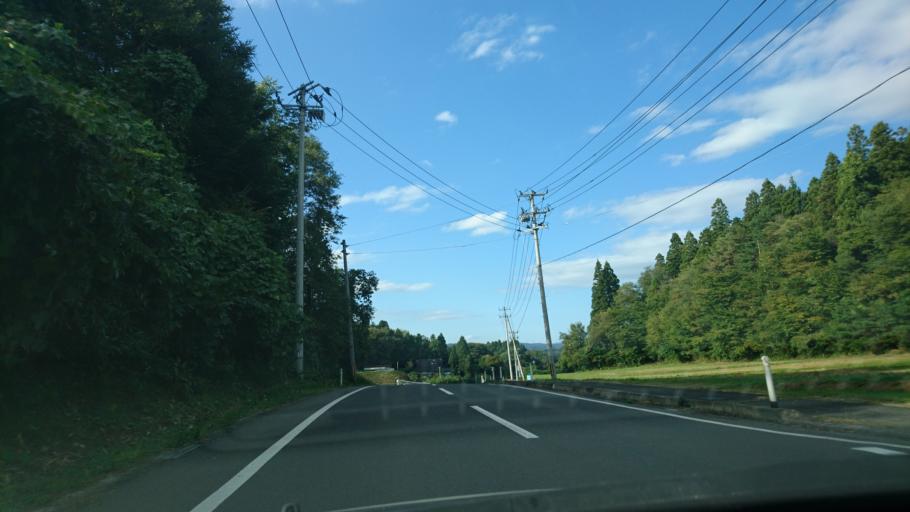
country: JP
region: Iwate
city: Ichinoseki
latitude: 38.8794
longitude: 141.3333
